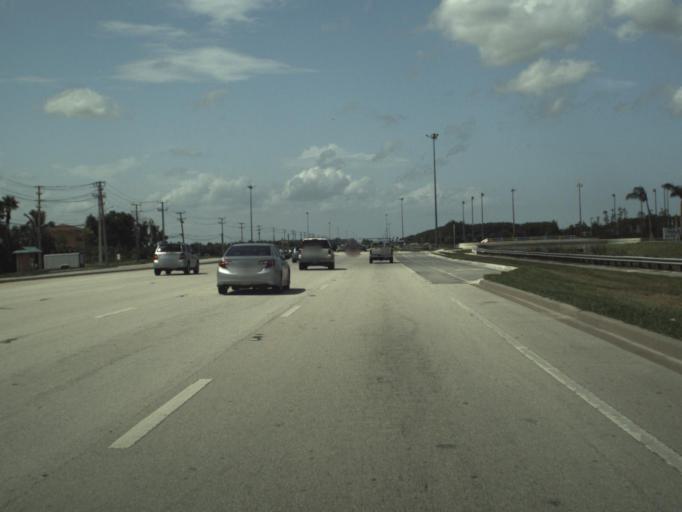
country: US
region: Florida
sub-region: Palm Beach County
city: Wellington
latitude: 26.6293
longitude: -80.2042
